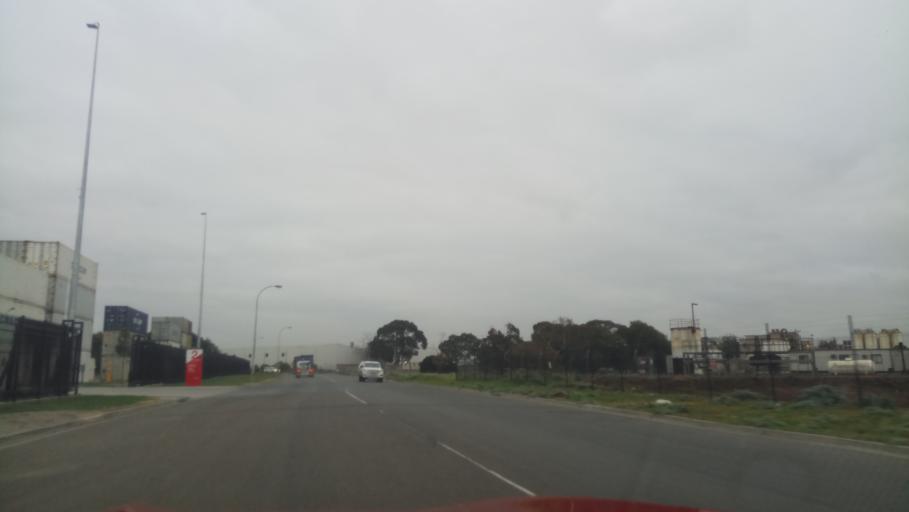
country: AU
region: Victoria
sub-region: Hobsons Bay
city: Laverton
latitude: -37.8524
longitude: 144.7954
